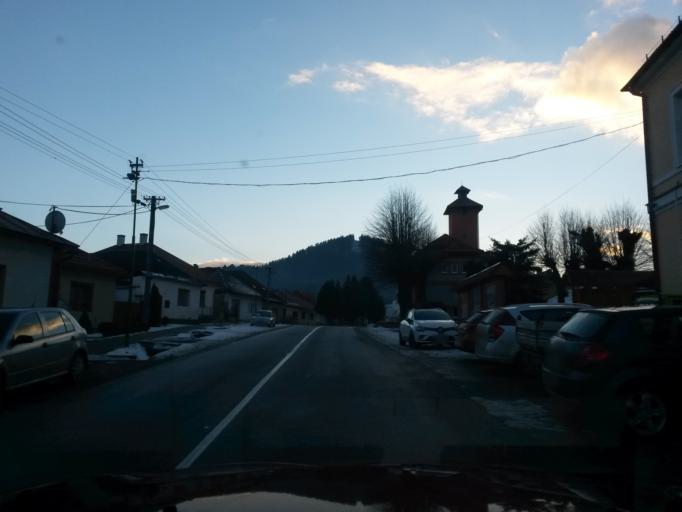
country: SK
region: Kosicky
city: Krompachy
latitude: 48.8061
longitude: 20.8067
